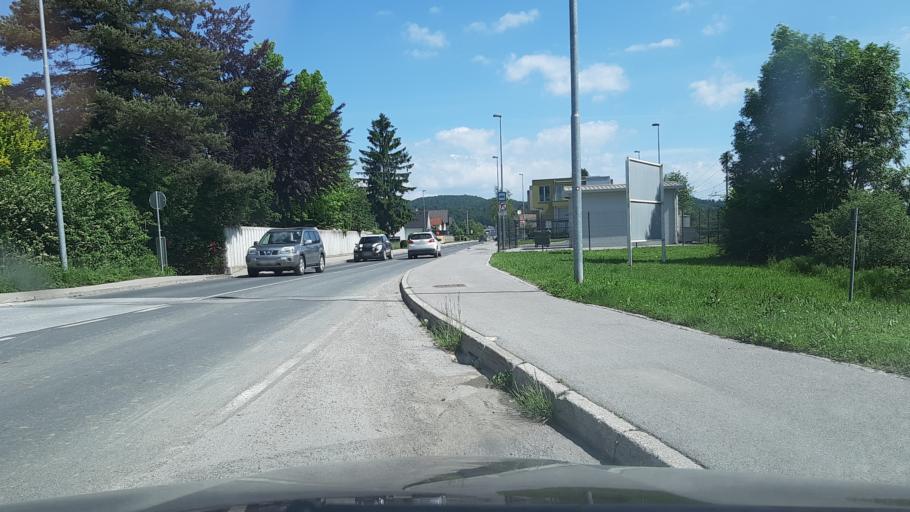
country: SI
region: Brezovica
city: Vnanje Gorice
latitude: 46.0110
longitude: 14.4126
